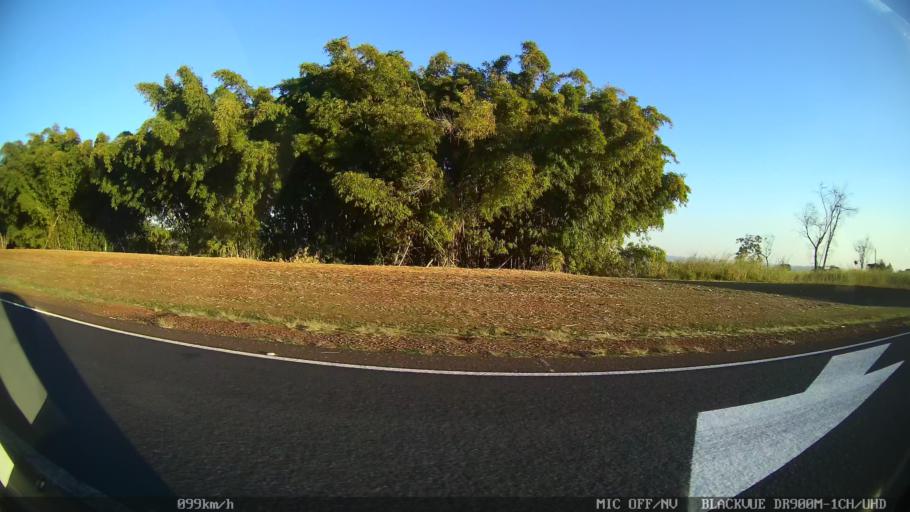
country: BR
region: Sao Paulo
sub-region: Araraquara
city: Araraquara
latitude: -21.8169
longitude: -48.2007
